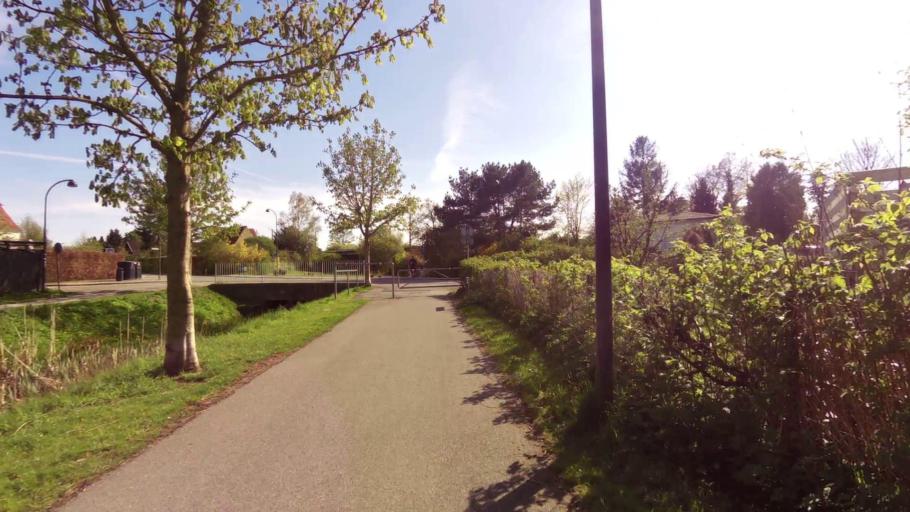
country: DK
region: Capital Region
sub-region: Lyngby-Tarbaek Kommune
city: Kongens Lyngby
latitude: 55.7351
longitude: 12.5351
